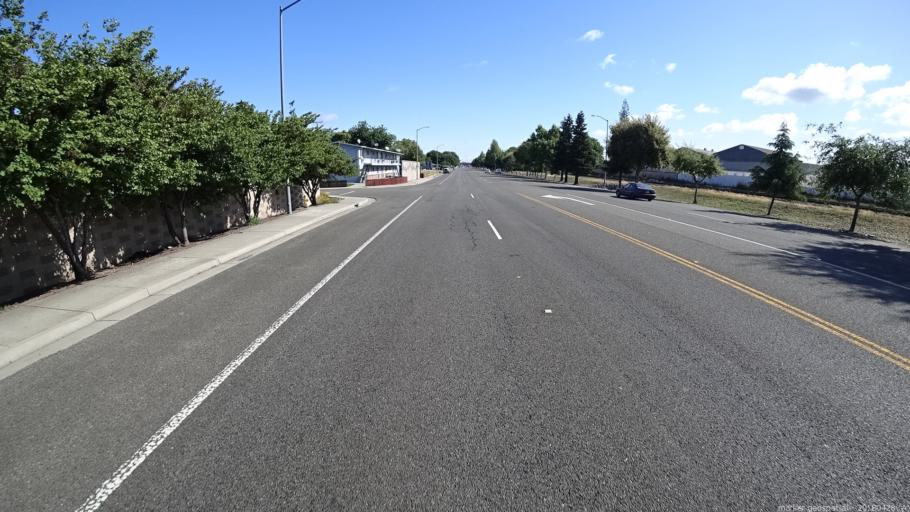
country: US
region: California
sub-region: Yolo County
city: West Sacramento
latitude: 38.5642
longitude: -121.5274
